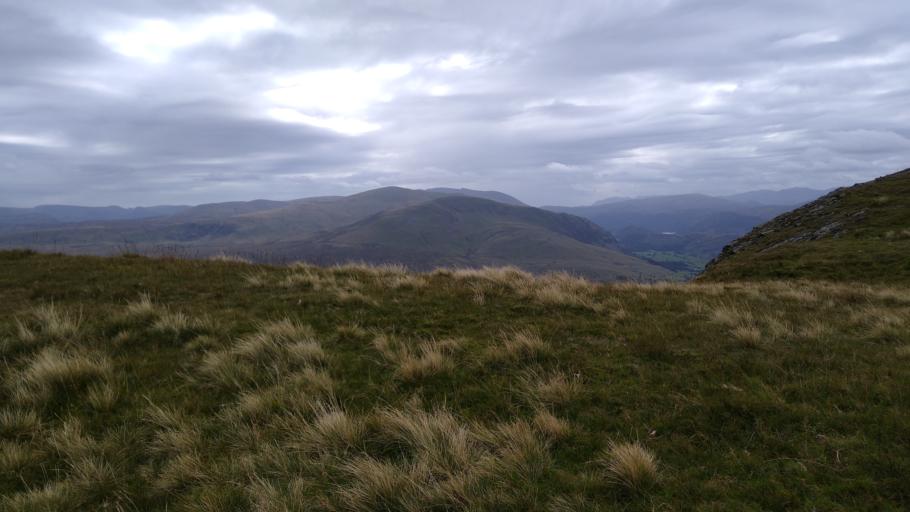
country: GB
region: England
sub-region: Cumbria
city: Keswick
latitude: 54.6414
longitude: -3.0387
